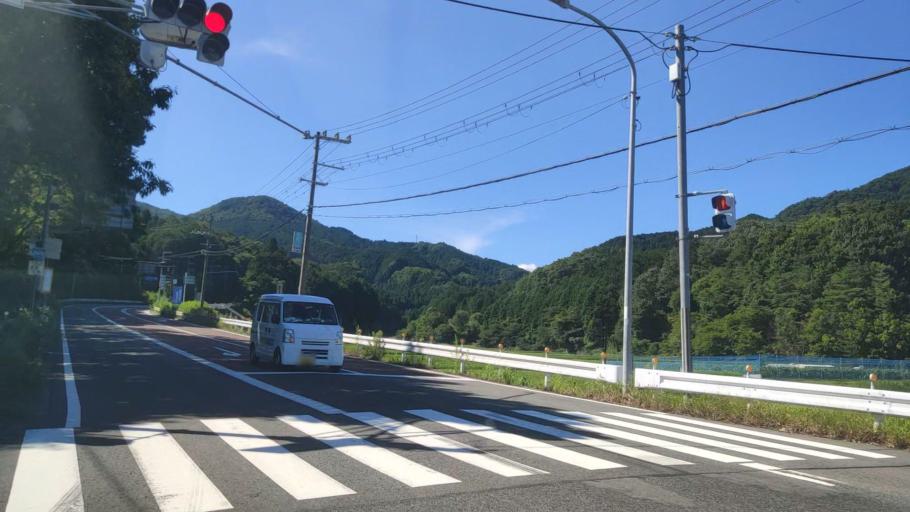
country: JP
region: Nara
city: Haibara-akanedai
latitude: 34.5479
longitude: 135.9613
